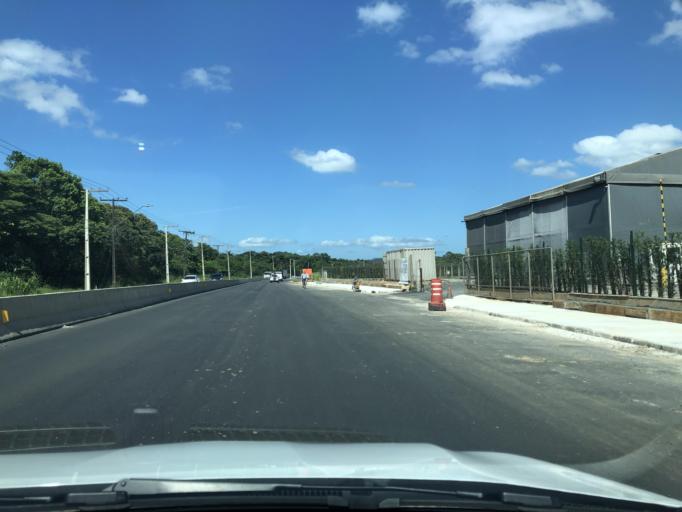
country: BR
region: Santa Catarina
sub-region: Joinville
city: Joinville
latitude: -26.2515
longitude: -48.8668
